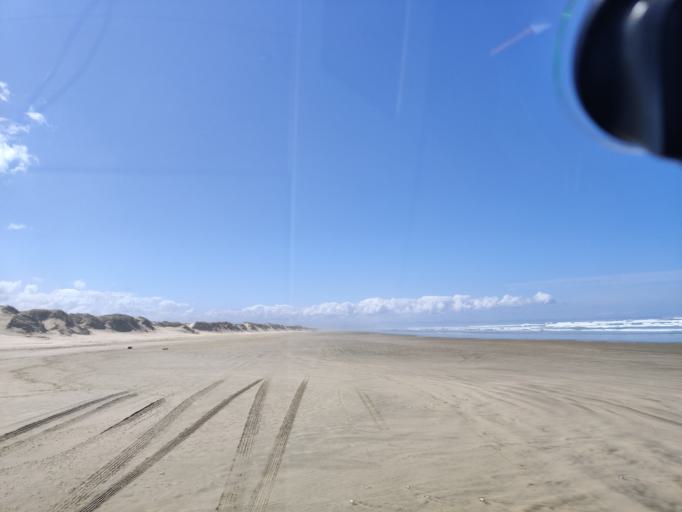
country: NZ
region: Northland
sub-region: Far North District
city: Kaitaia
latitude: -34.9087
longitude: 173.0914
